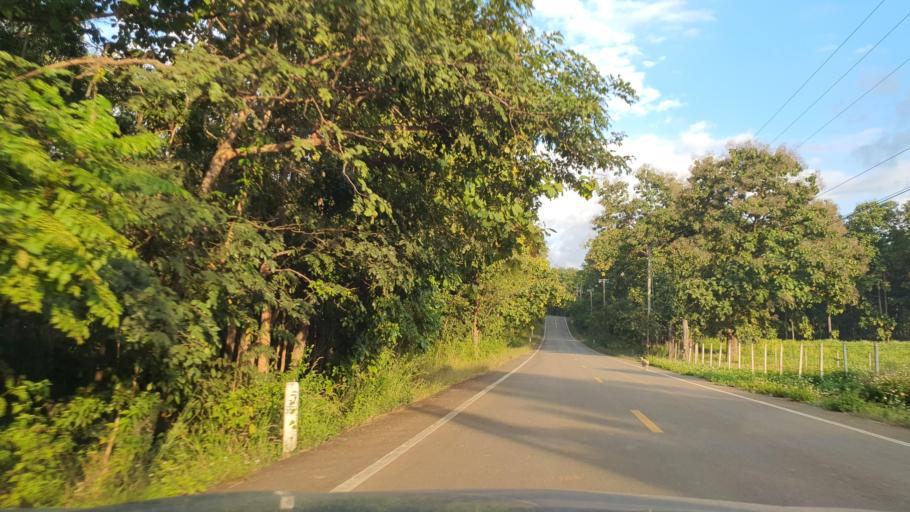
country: TH
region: Chiang Mai
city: Mae On
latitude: 18.8548
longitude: 99.2493
